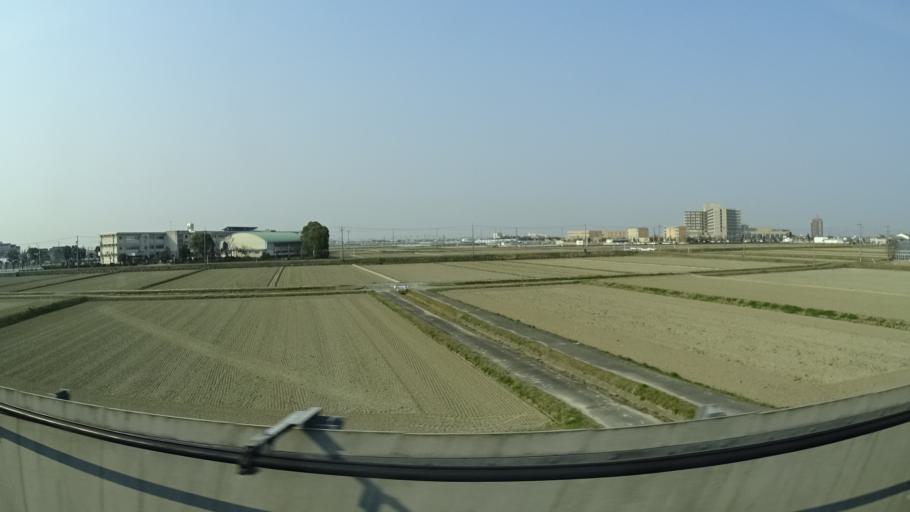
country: JP
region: Aichi
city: Anjo
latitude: 34.9407
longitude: 137.0865
